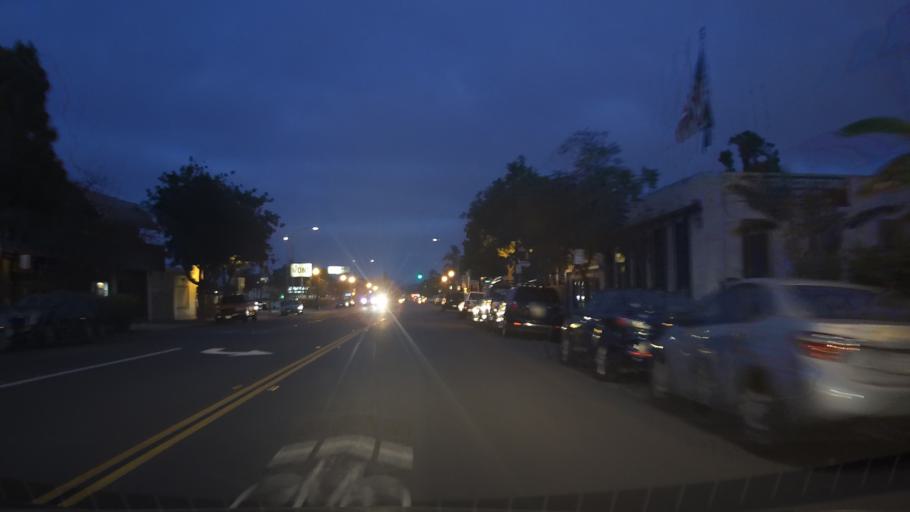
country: US
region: California
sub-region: San Diego County
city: San Diego
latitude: 32.7633
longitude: -117.1162
